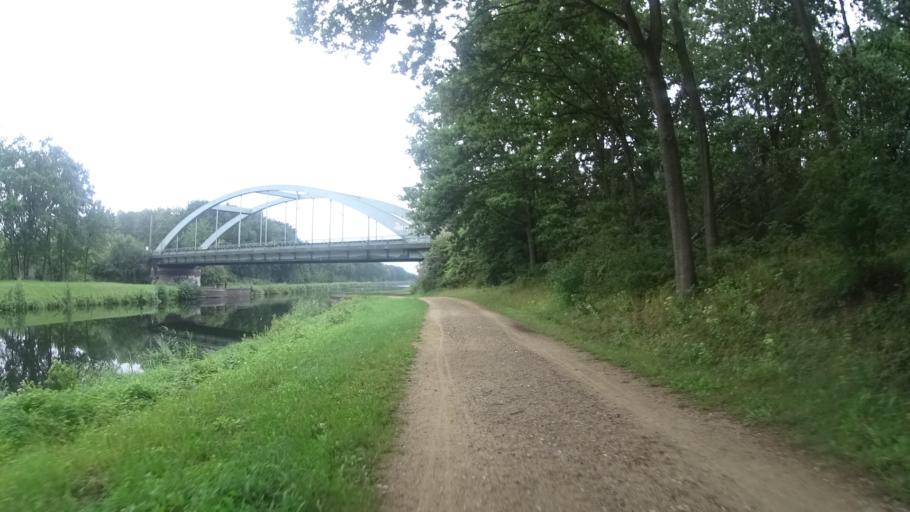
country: DE
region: Schleswig-Holstein
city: Buchen
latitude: 53.4722
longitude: 10.6302
